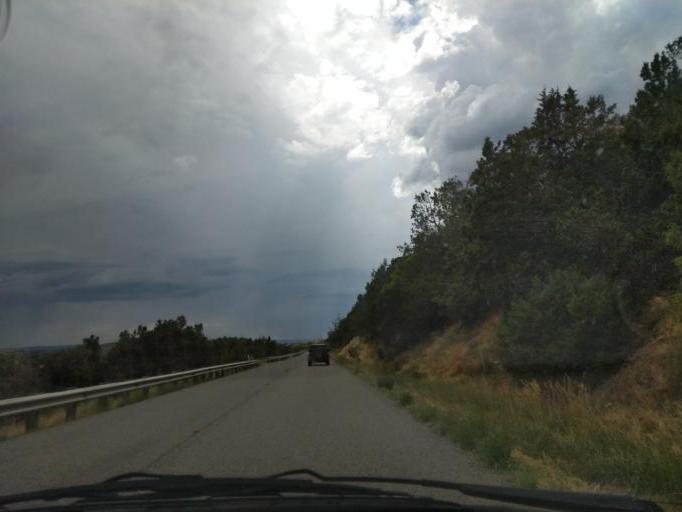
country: US
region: Colorado
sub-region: Delta County
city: Paonia
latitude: 38.8950
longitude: -107.5736
